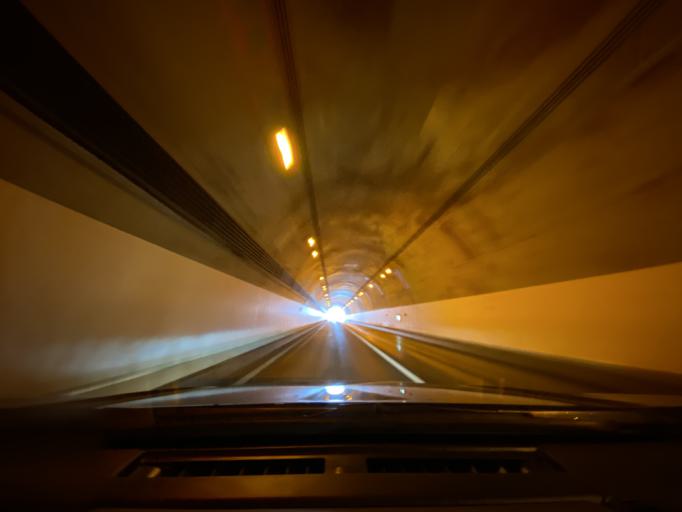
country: JP
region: Hokkaido
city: Rumoi
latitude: 43.8189
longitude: 141.4260
